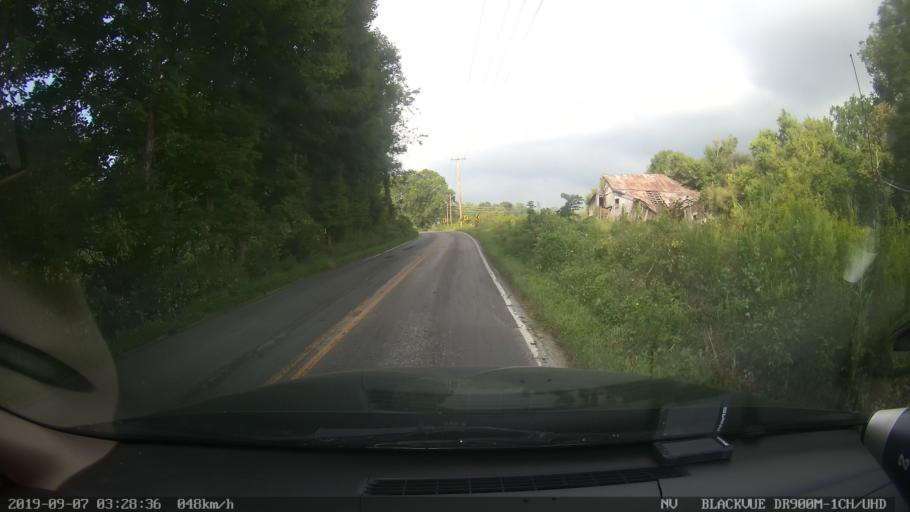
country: US
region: Ohio
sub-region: Licking County
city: Granville
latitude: 40.1229
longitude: -82.5154
